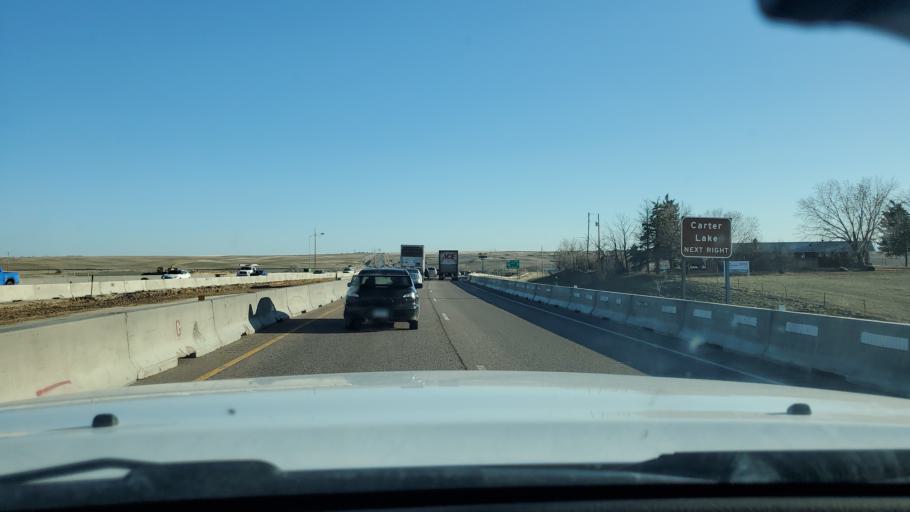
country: US
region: Colorado
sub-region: Weld County
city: Johnstown
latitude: 40.3116
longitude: -104.9809
